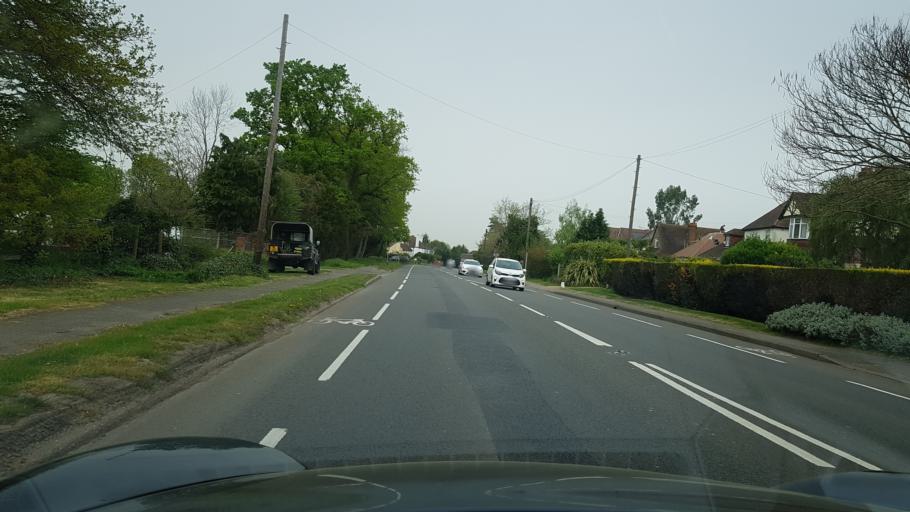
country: GB
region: England
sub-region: Surrey
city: Ripley
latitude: 51.2913
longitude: -0.5022
